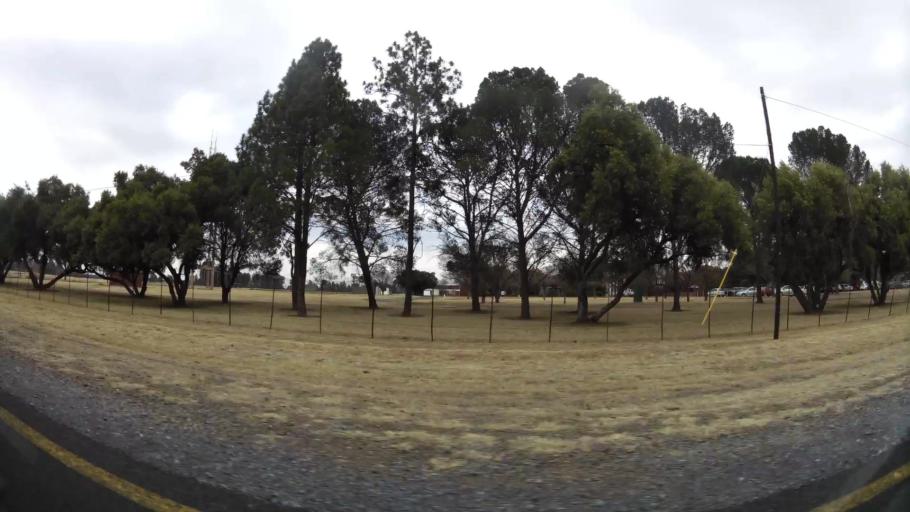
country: ZA
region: Orange Free State
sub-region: Fezile Dabi District Municipality
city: Kroonstad
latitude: -27.6240
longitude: 27.2329
